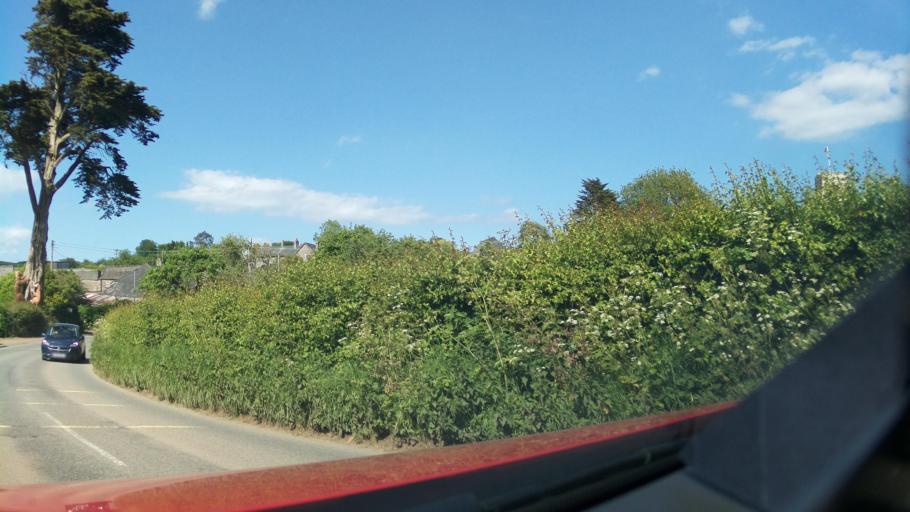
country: GB
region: England
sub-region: Devon
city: Totnes
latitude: 50.4371
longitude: -3.6531
